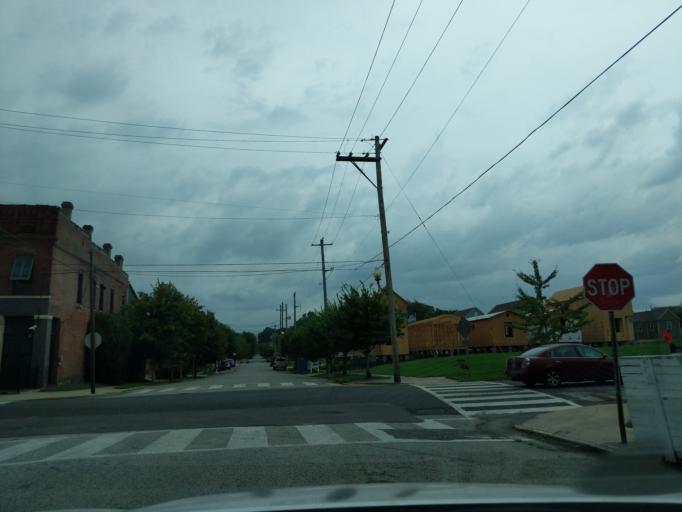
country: US
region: Tennessee
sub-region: Shelby County
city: Memphis
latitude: 35.1612
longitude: -90.0467
